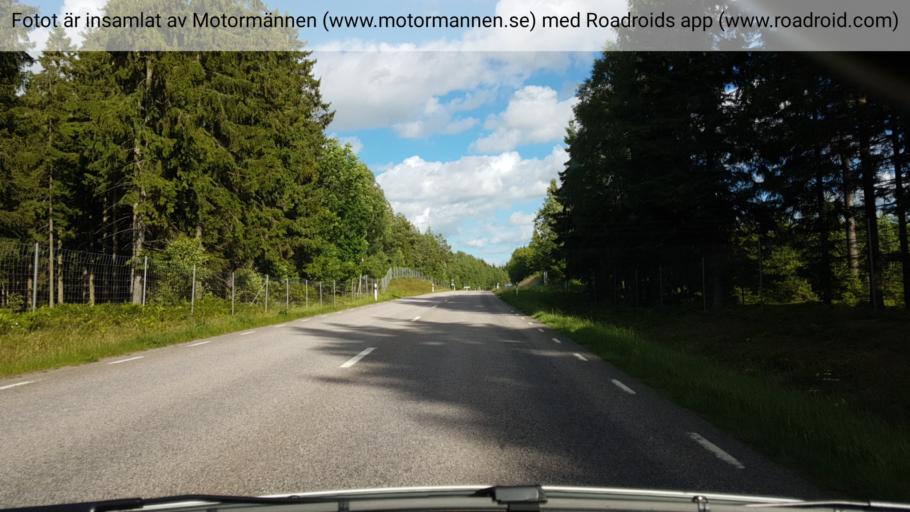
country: SE
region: Vaestra Goetaland
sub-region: Falkopings Kommun
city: Floby
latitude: 58.2048
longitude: 13.3020
